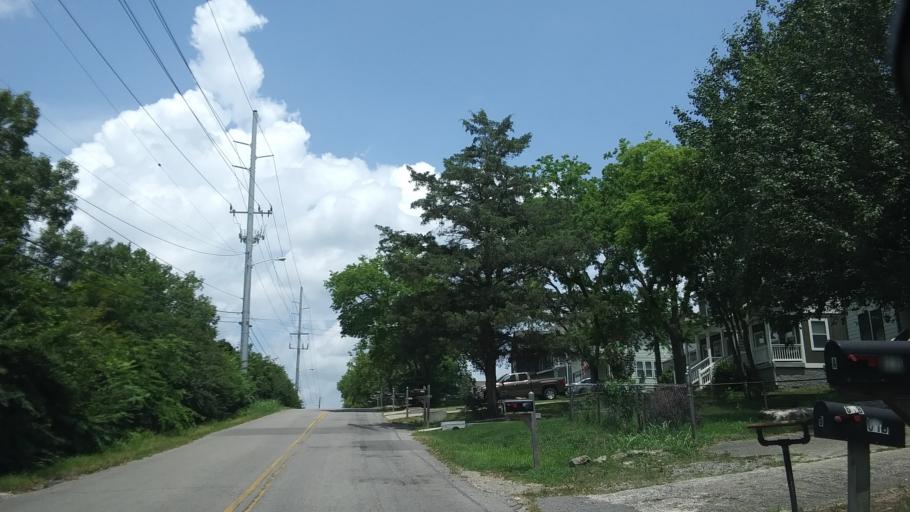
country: US
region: Tennessee
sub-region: Davidson County
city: Belle Meade
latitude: 36.1603
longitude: -86.8772
